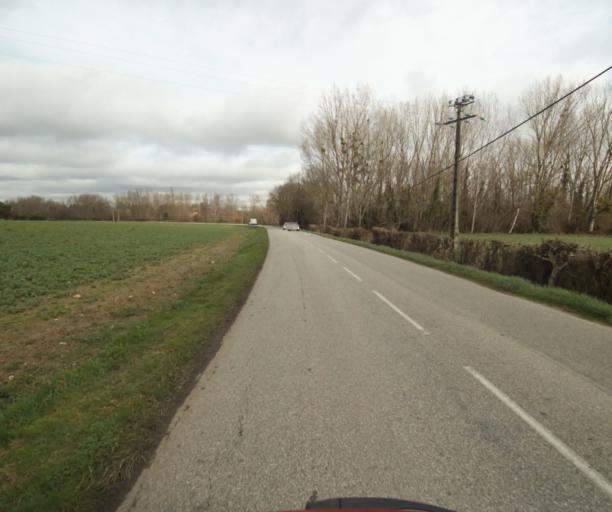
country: FR
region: Midi-Pyrenees
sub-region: Departement de l'Ariege
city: Pamiers
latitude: 43.1268
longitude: 1.6044
